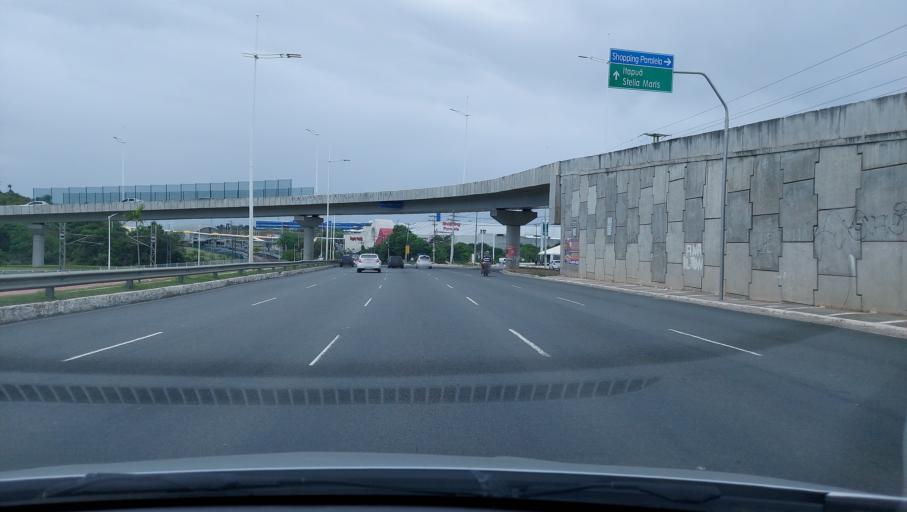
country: BR
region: Bahia
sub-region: Lauro De Freitas
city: Lauro de Freitas
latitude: -12.9376
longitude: -38.3991
